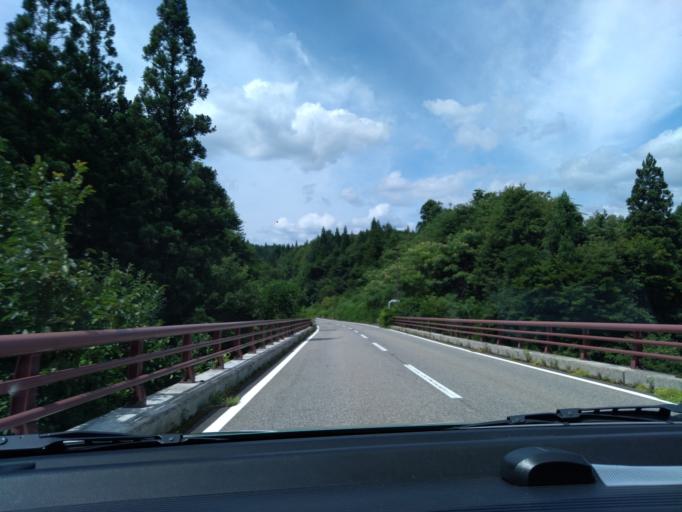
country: JP
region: Akita
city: Akita
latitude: 39.6514
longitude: 140.3171
